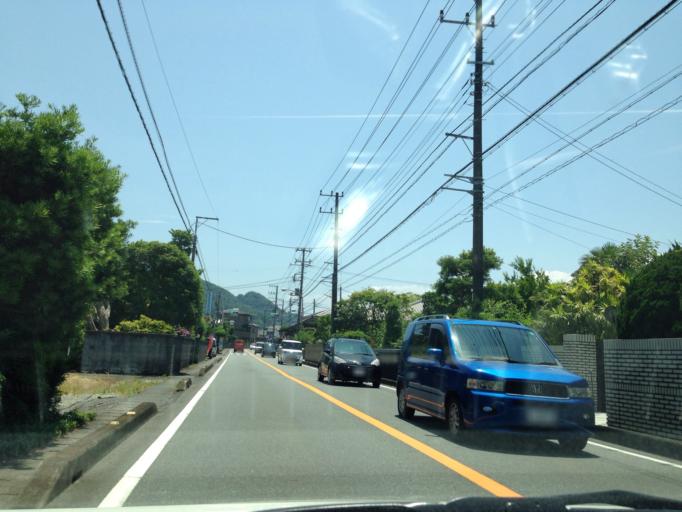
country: JP
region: Shizuoka
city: Numazu
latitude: 35.0704
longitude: 138.8760
